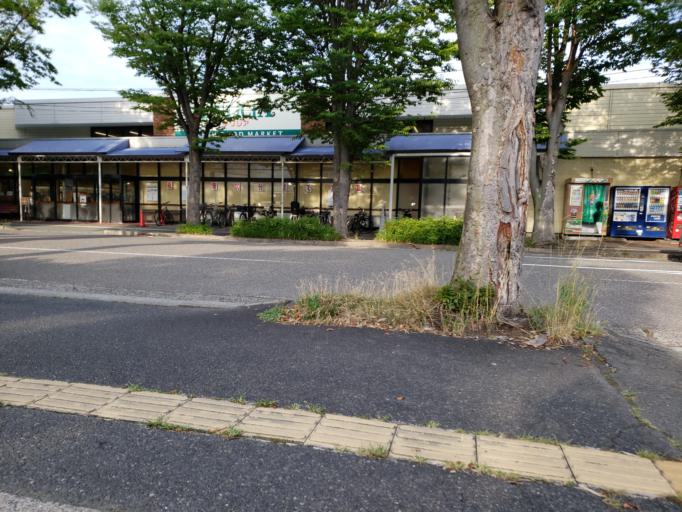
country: JP
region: Nagano
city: Nagano-shi
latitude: 36.6323
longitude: 138.1877
